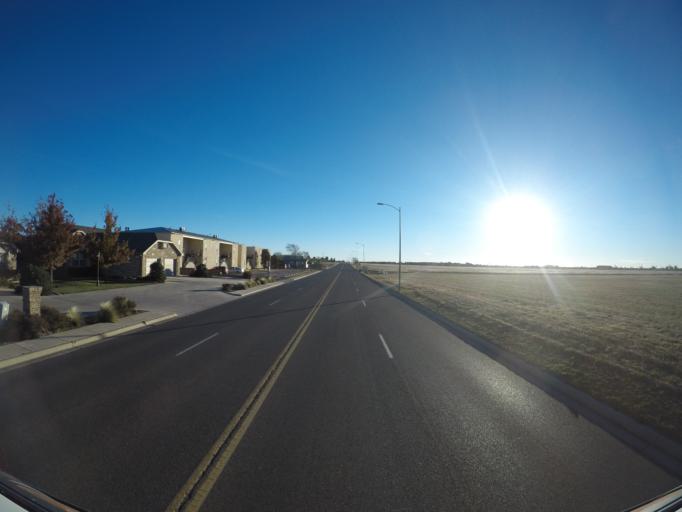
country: US
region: New Mexico
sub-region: Curry County
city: Clovis
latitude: 34.4048
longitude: -103.1766
